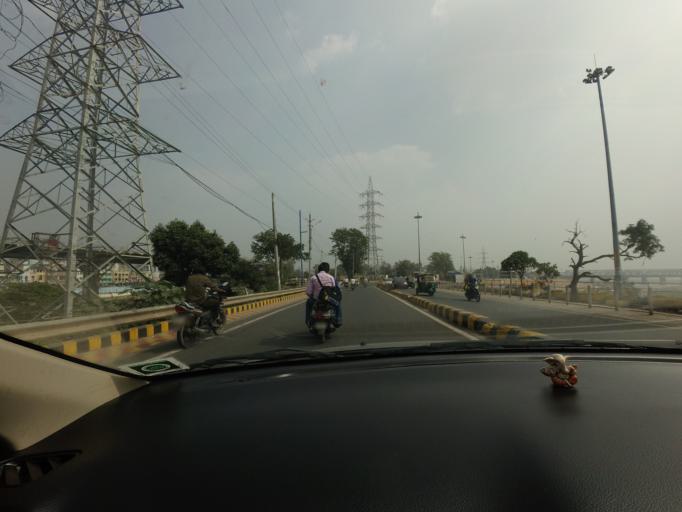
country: IN
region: Andhra Pradesh
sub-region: Krishna
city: Vijayawada
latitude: 16.5112
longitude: 80.6087
